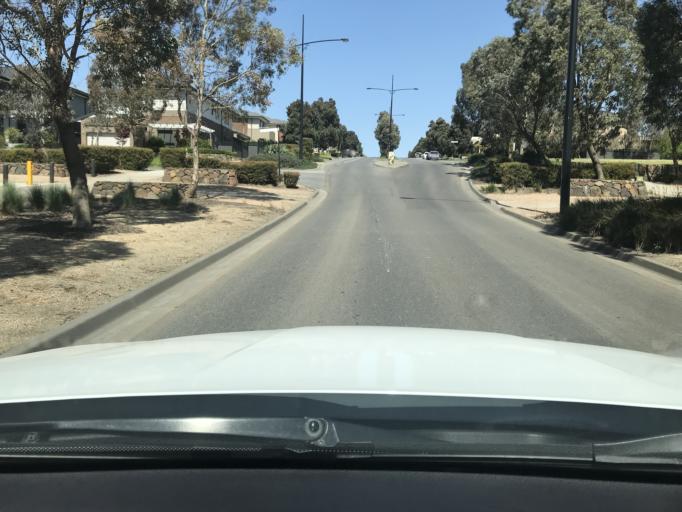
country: AU
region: Victoria
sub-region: Hume
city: Roxburgh Park
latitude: -37.5966
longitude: 144.9045
